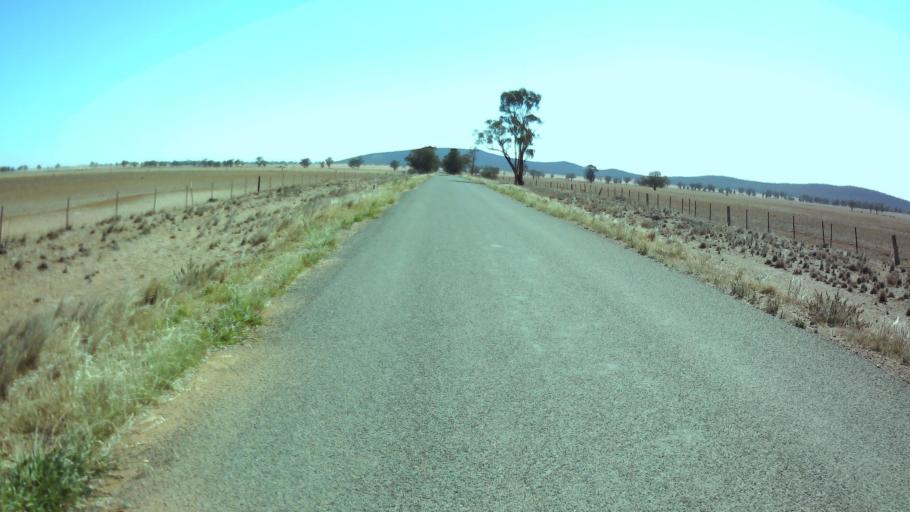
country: AU
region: New South Wales
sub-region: Weddin
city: Grenfell
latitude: -33.7127
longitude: 147.9093
